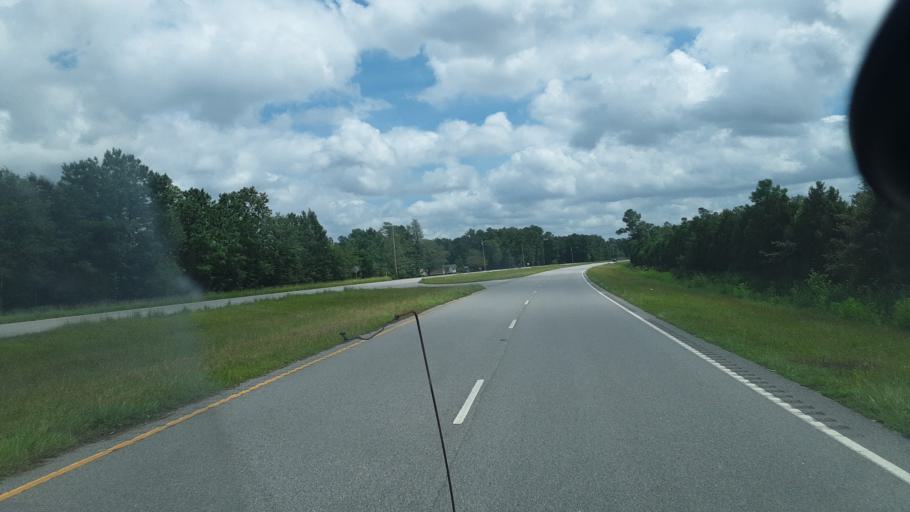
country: US
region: South Carolina
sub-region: Horry County
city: Loris
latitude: 34.1071
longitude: -78.9333
